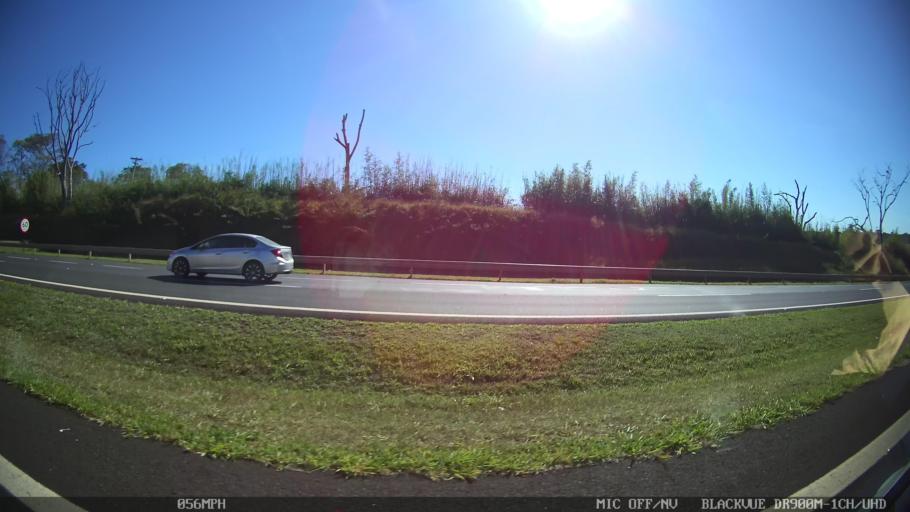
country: BR
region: Sao Paulo
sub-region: Franca
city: Franca
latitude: -20.5755
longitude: -47.3638
